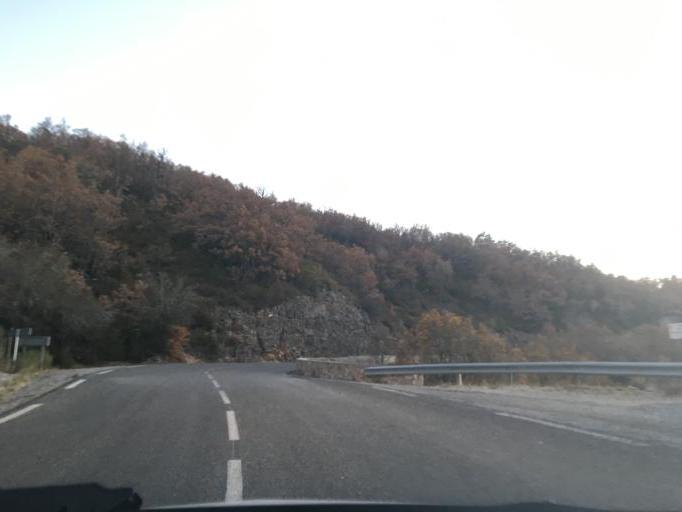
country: FR
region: Provence-Alpes-Cote d'Azur
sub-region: Departement du Var
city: Montferrat
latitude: 43.6695
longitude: 6.4913
